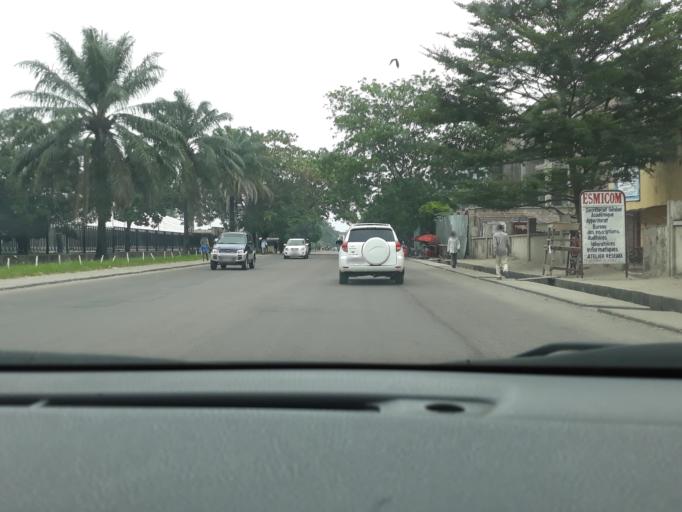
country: CD
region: Kinshasa
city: Kinshasa
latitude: -4.3303
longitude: 15.3039
